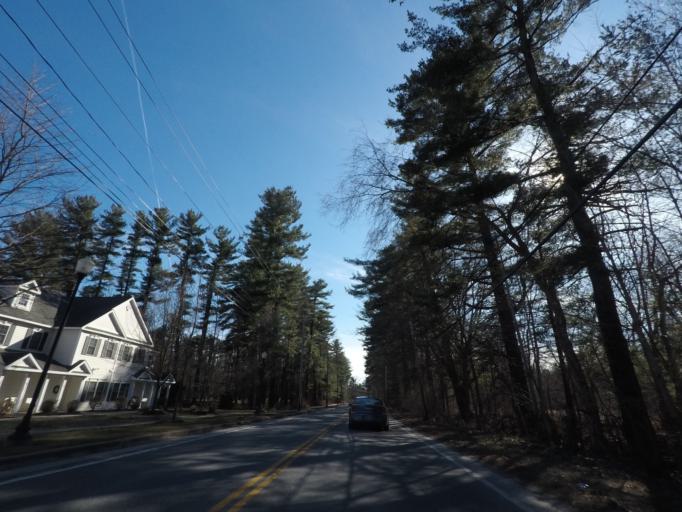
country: US
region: New York
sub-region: Saratoga County
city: Saratoga Springs
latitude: 43.0645
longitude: -73.7984
